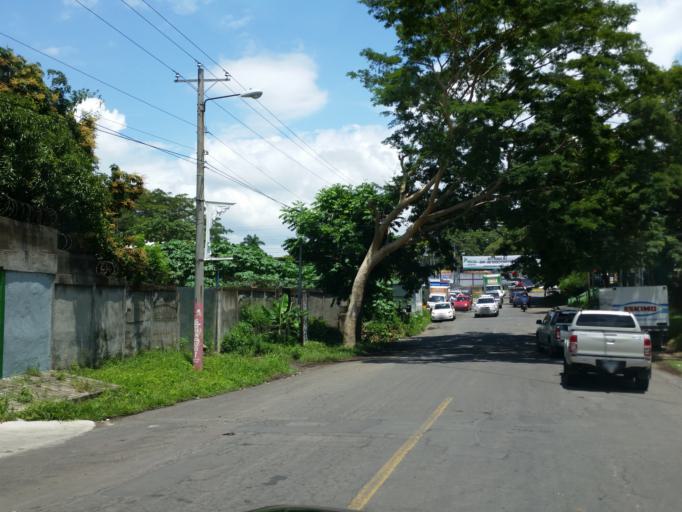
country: NI
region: Managua
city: Managua
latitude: 12.0945
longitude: -86.2399
